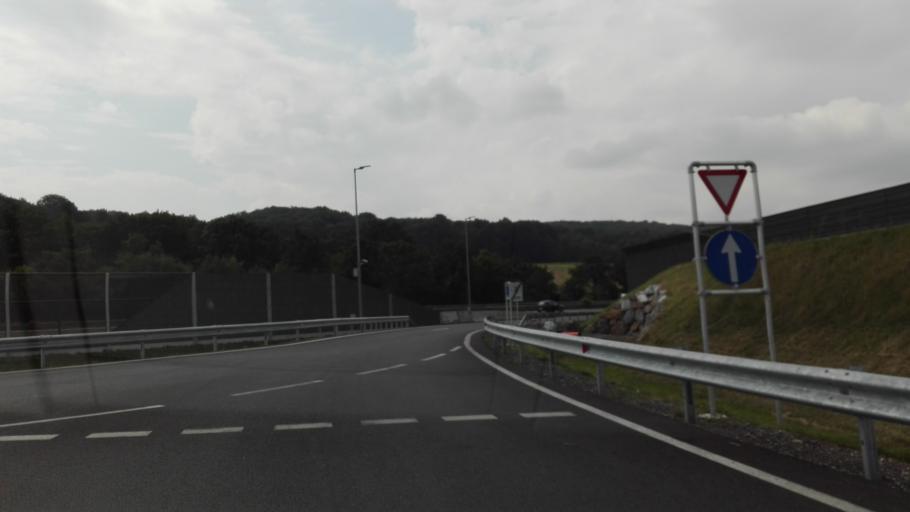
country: AT
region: Lower Austria
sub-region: Politischer Bezirk Melk
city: Klein-Poechlarn
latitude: 48.1993
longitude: 15.2547
